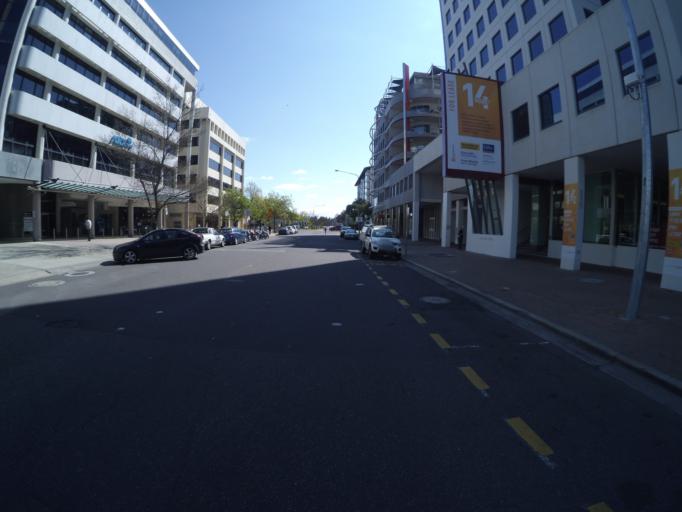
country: AU
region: Australian Capital Territory
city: Canberra
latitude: -35.2764
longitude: 149.1283
